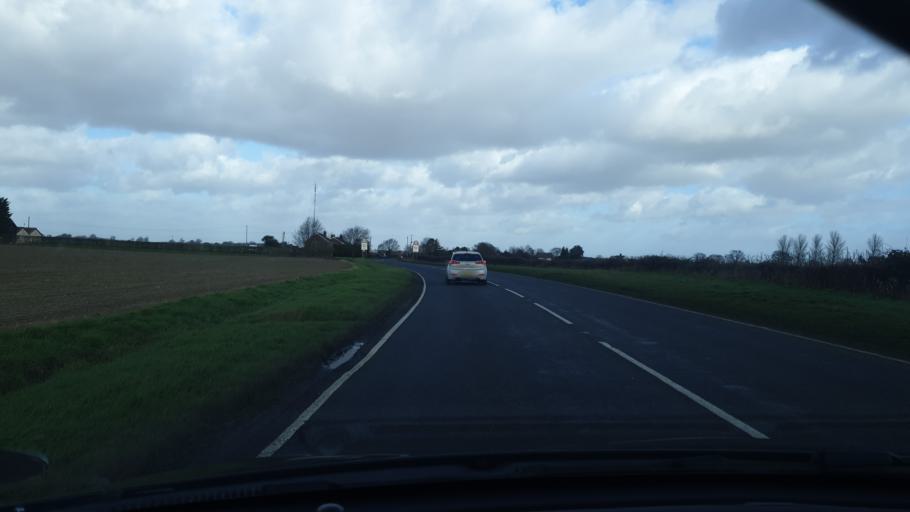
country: GB
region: England
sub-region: Essex
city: Mistley
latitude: 51.9093
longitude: 1.0817
